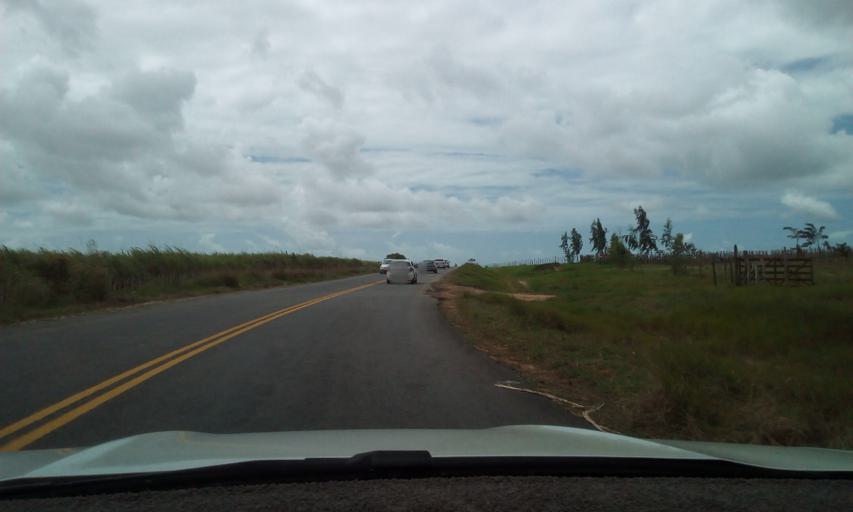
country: BR
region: Paraiba
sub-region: Rio Tinto
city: Rio Tinto
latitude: -6.7741
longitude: -35.0431
